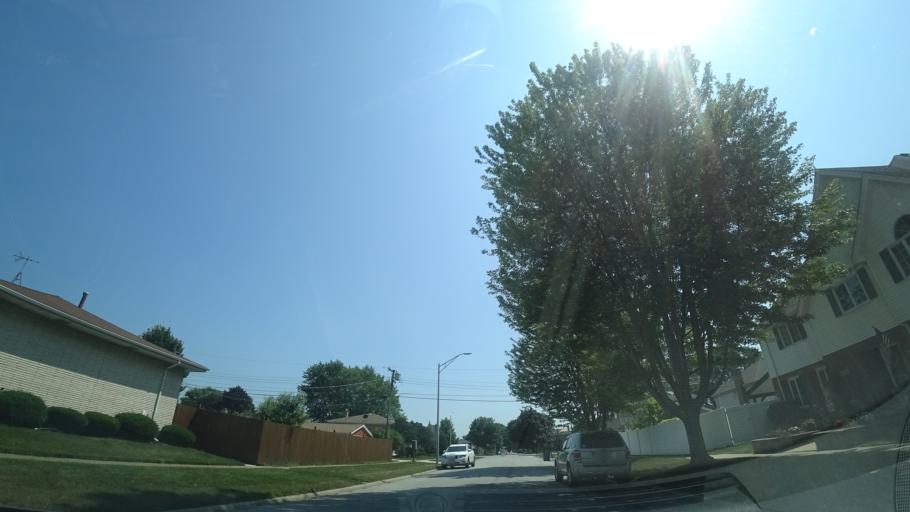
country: US
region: Illinois
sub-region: Cook County
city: Oak Lawn
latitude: 41.6999
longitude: -87.7425
